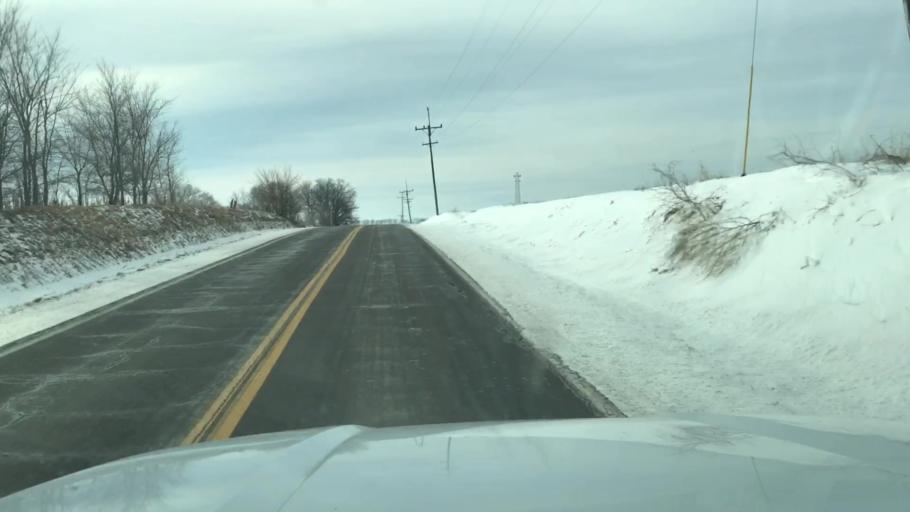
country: US
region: Missouri
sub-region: Holt County
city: Oregon
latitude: 40.0527
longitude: -95.1357
